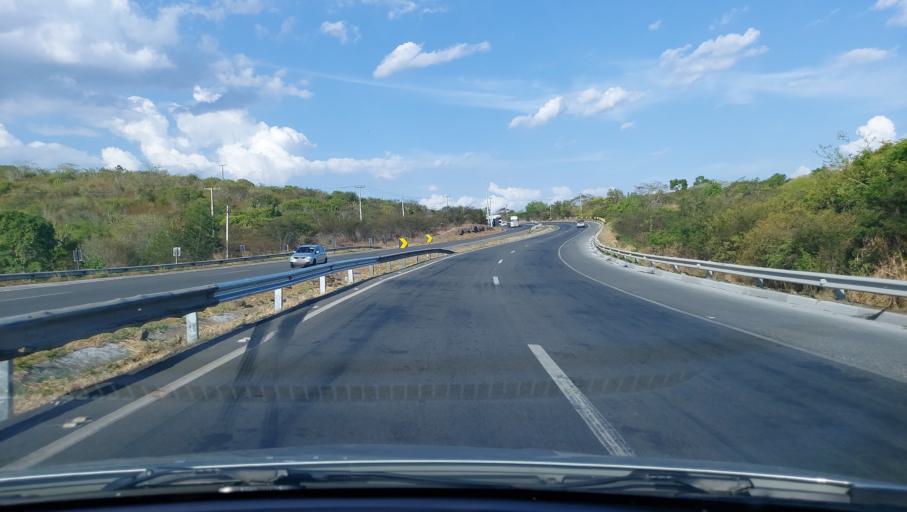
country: BR
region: Bahia
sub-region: Sao Goncalo Dos Campos
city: Sao Goncalo dos Campos
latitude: -12.3528
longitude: -39.0933
